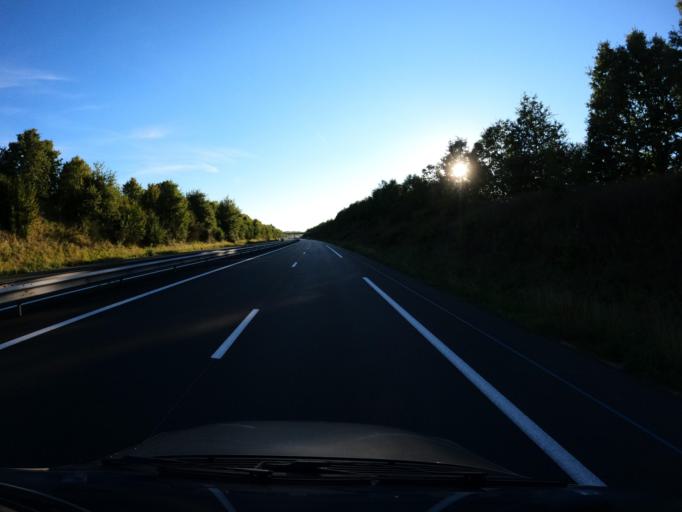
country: FR
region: Pays de la Loire
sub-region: Departement de la Vendee
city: Beaurepaire
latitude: 46.8887
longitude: -1.0996
